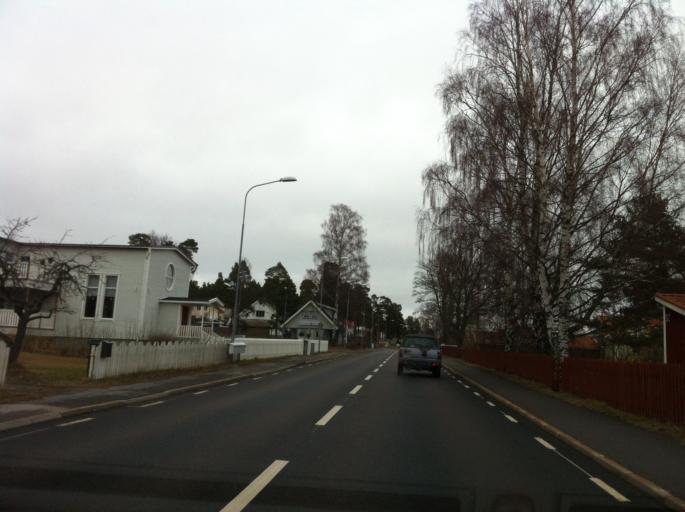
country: SE
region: Kalmar
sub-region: Vasterviks Kommun
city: Overum
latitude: 57.9082
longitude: 16.2421
